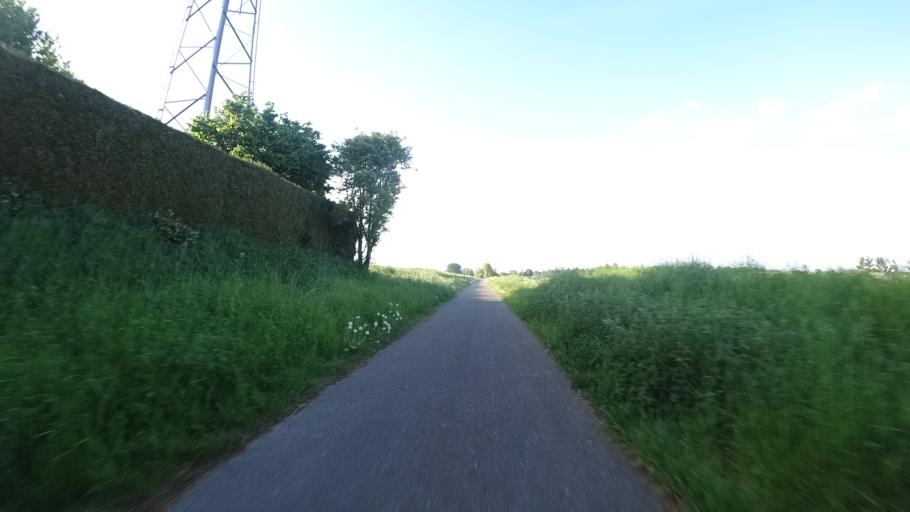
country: BE
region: Wallonia
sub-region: Province de Namur
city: Eghezee
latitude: 50.5373
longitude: 4.9015
